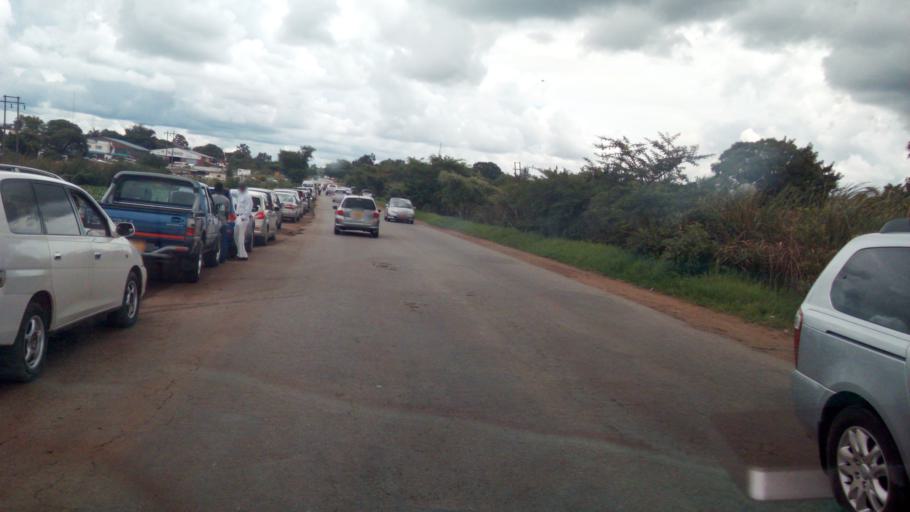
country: ZW
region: Harare
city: Harare
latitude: -17.7903
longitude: 30.9881
